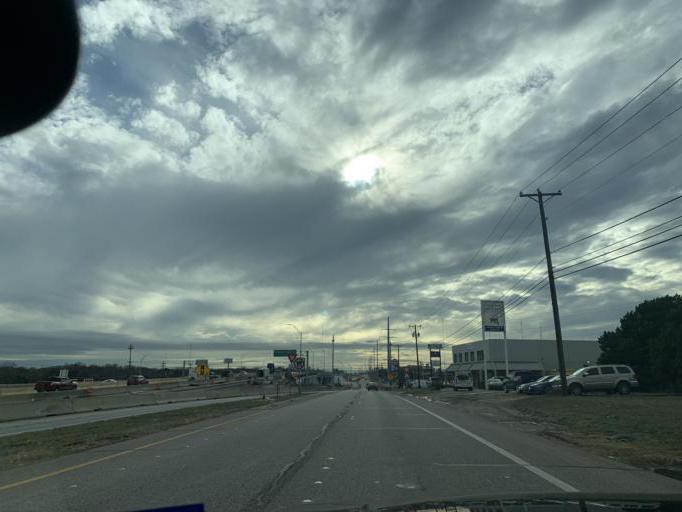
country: US
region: Texas
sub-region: Dallas County
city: Shamrock
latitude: 32.6124
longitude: -96.9235
